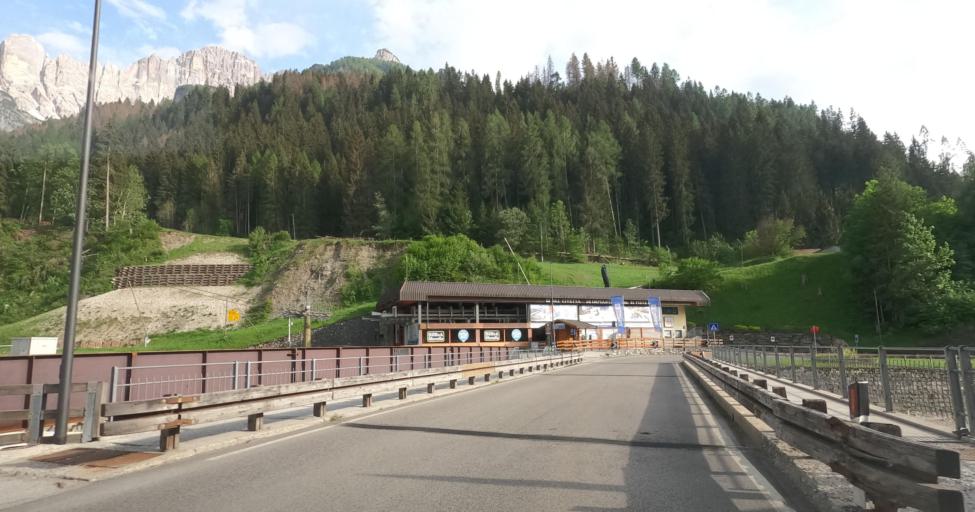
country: IT
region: Veneto
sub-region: Provincia di Belluno
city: Alleghe
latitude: 46.4058
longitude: 12.0232
